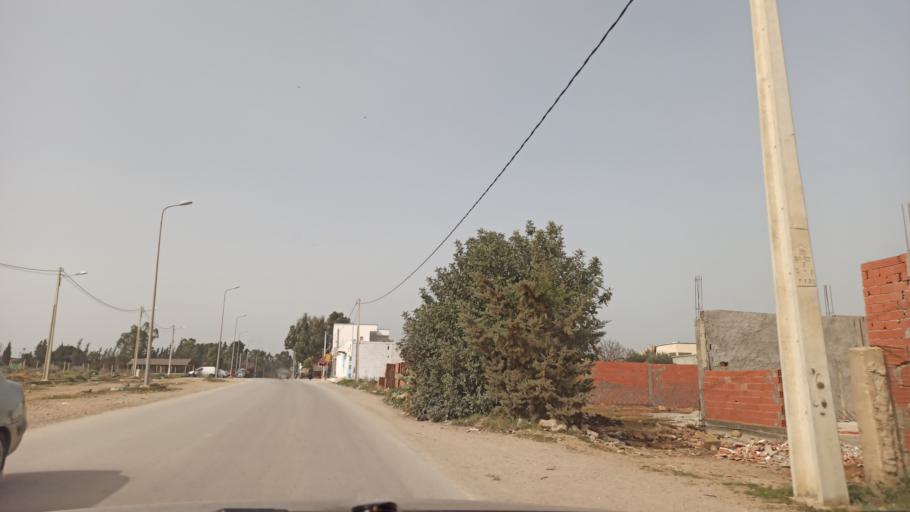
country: TN
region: Zaghwan
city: Zaghouan
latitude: 36.4160
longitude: 10.1276
